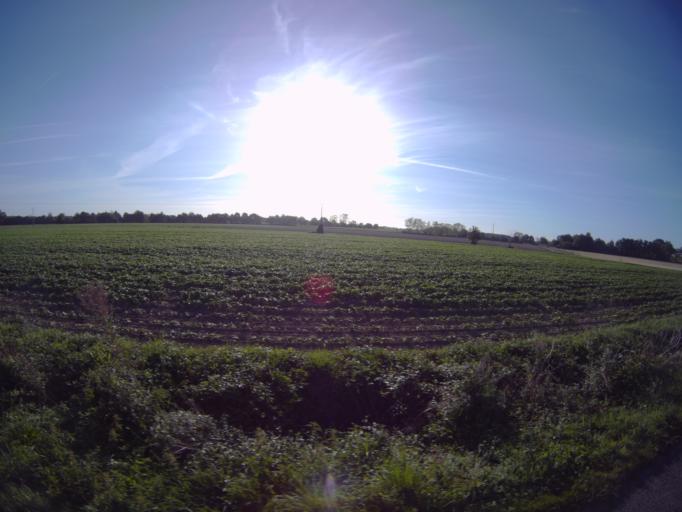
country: FR
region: Pays de la Loire
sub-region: Departement de la Loire-Atlantique
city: La Planche
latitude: 47.0016
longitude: -1.4553
